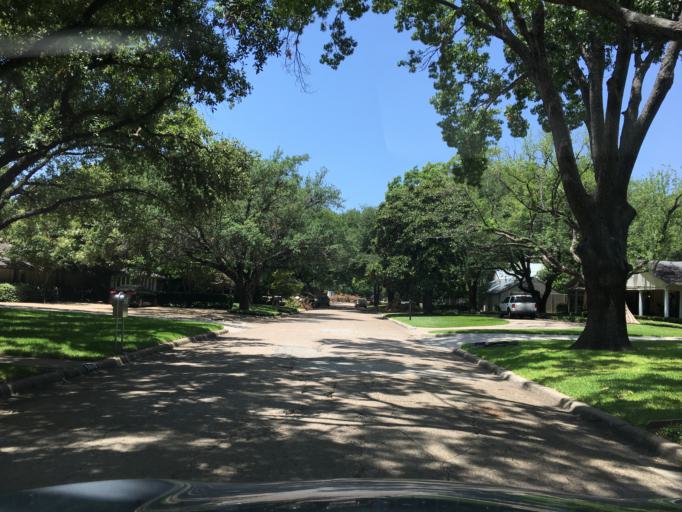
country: US
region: Texas
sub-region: Dallas County
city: University Park
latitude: 32.8811
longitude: -96.8073
